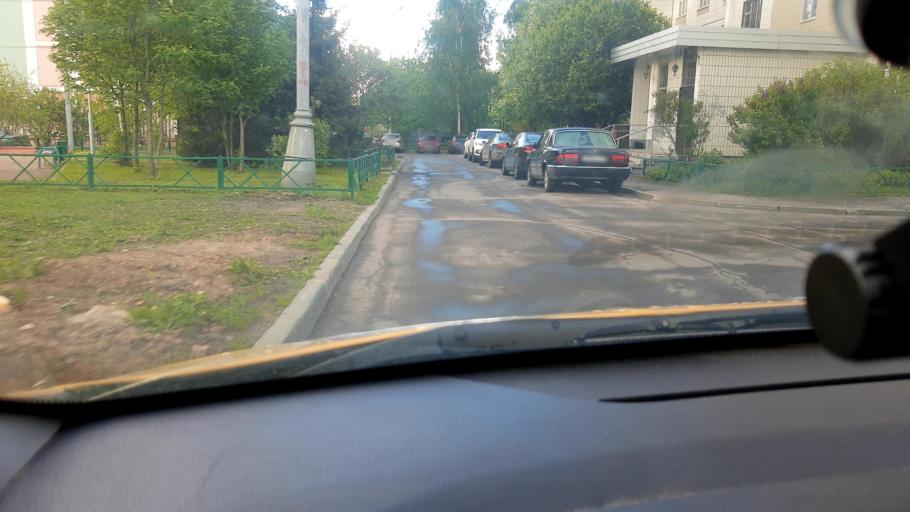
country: RU
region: Moskovskaya
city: Kommunarka
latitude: 55.5468
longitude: 37.5205
